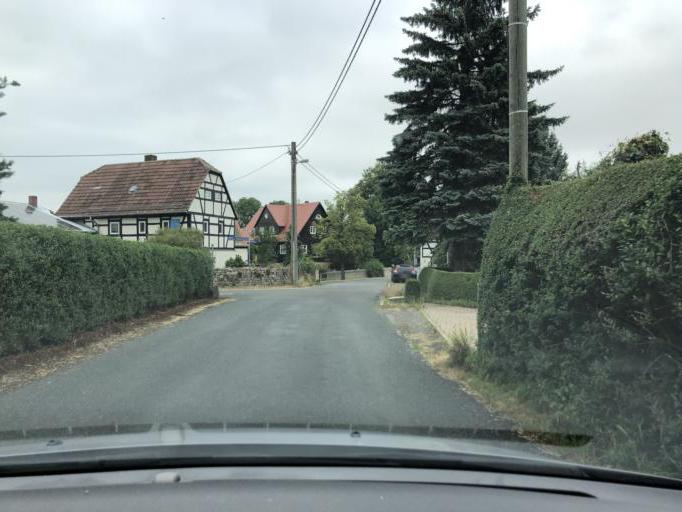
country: DE
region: Saxony
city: Frohburg
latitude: 51.0973
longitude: 12.5594
